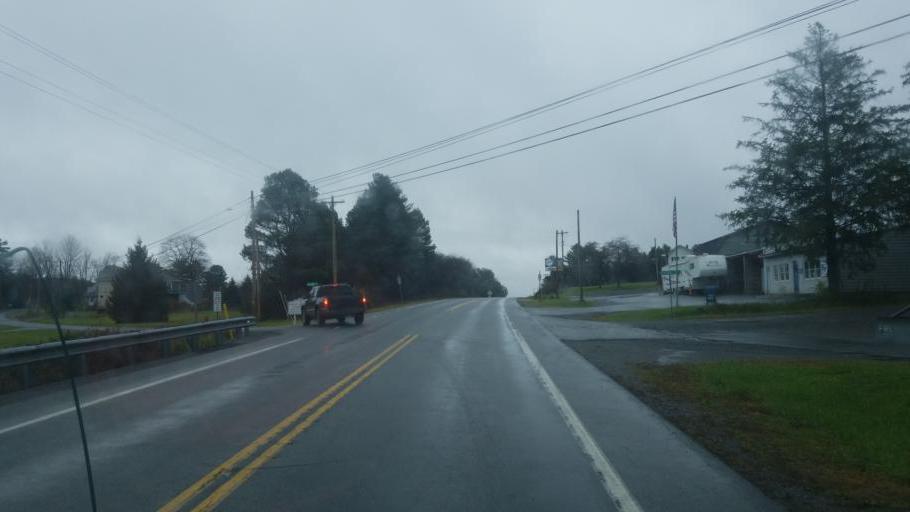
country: US
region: Pennsylvania
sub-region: Clearfield County
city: Shiloh
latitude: 41.1041
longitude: -78.2275
